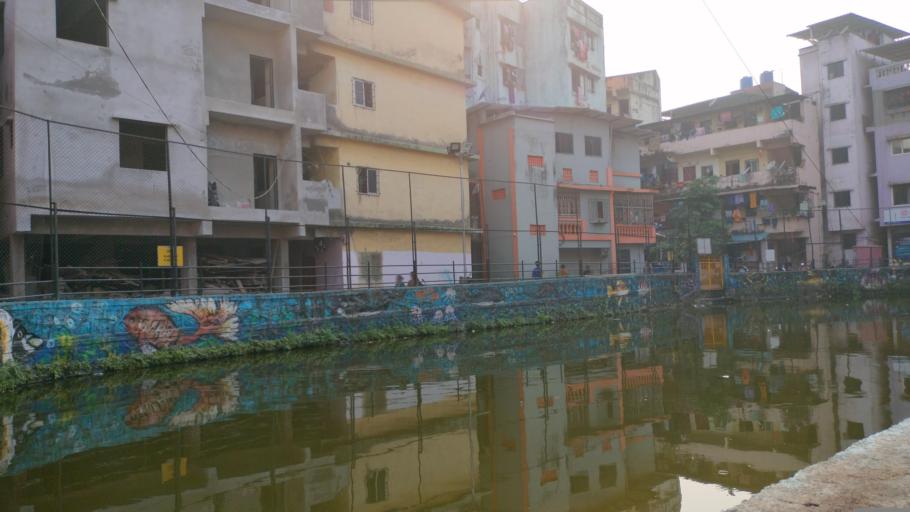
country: IN
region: Maharashtra
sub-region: Thane
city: Navi Mumbai
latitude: 19.0855
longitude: 73.0011
